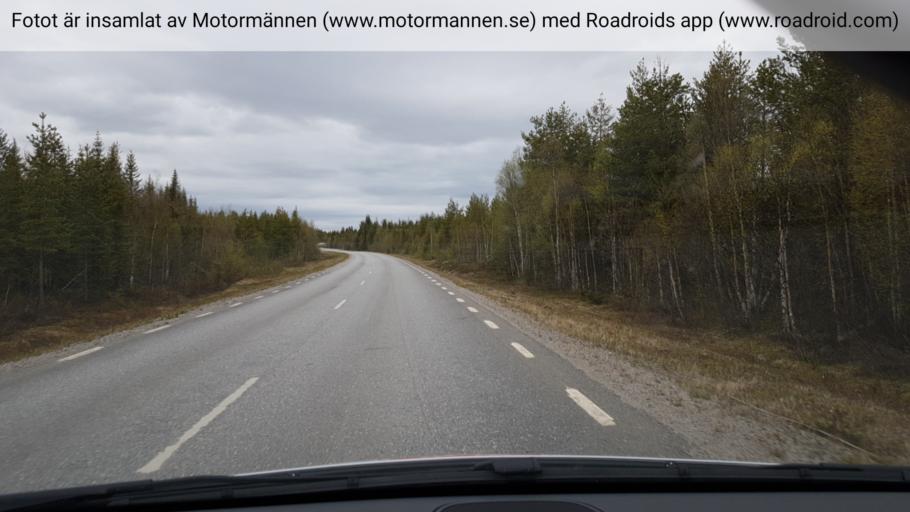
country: SE
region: Vaesterbotten
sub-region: Sorsele Kommun
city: Sorsele
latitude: 65.5082
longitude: 17.2926
